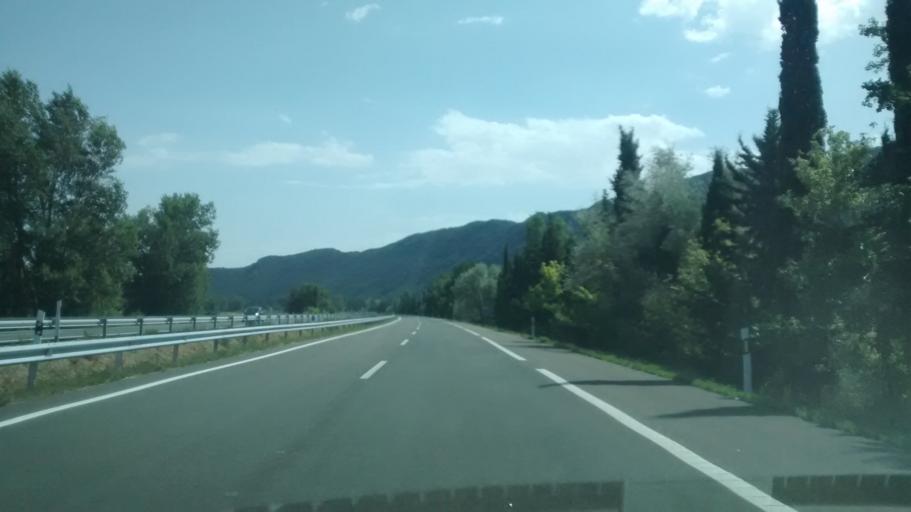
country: ES
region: Basque Country
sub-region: Provincia de Alava
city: Zambrana
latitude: 42.6549
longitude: -2.8862
